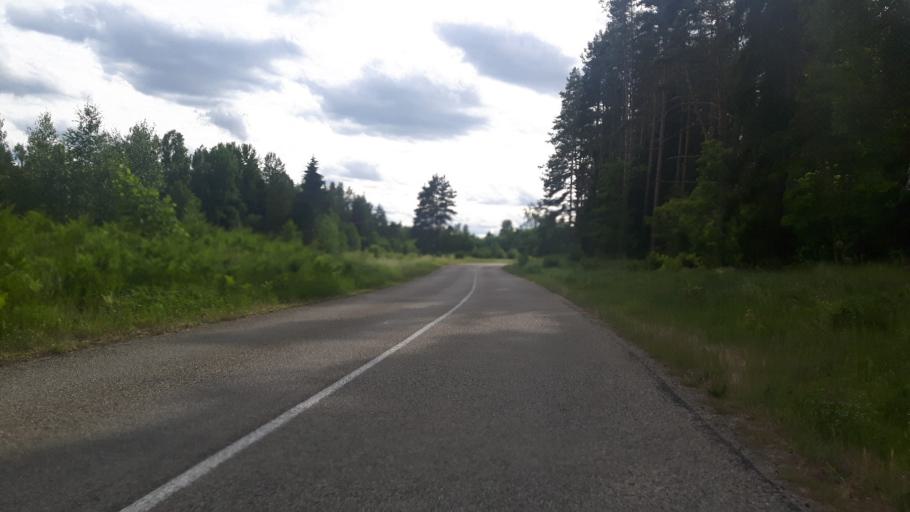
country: LV
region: Engure
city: Smarde
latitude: 56.9914
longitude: 23.3084
